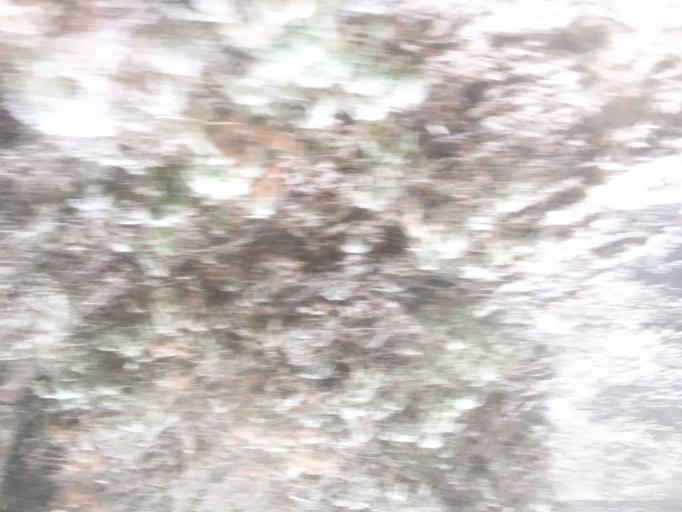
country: JP
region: Aomori
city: Goshogawara
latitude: 41.0991
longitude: 140.5283
